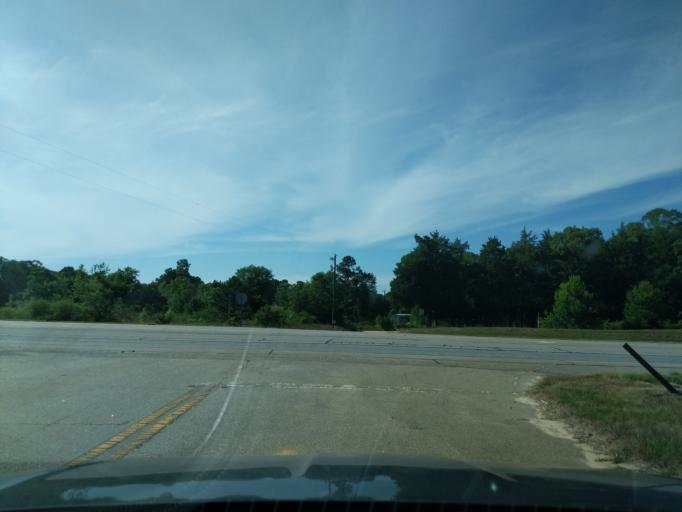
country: US
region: Georgia
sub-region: Jefferson County
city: Wrens
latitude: 33.2309
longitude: -82.3552
